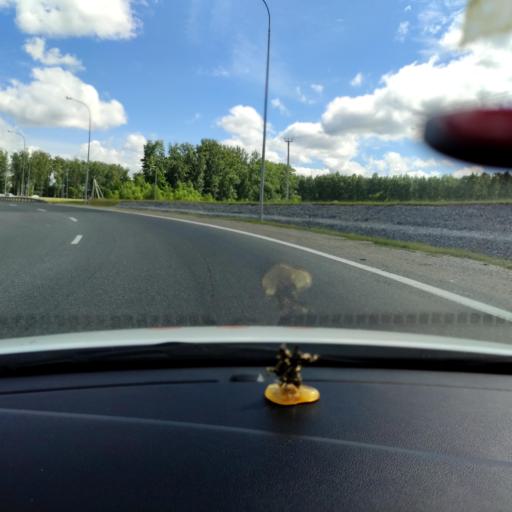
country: RU
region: Tatarstan
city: Aysha
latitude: 55.8698
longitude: 48.6624
